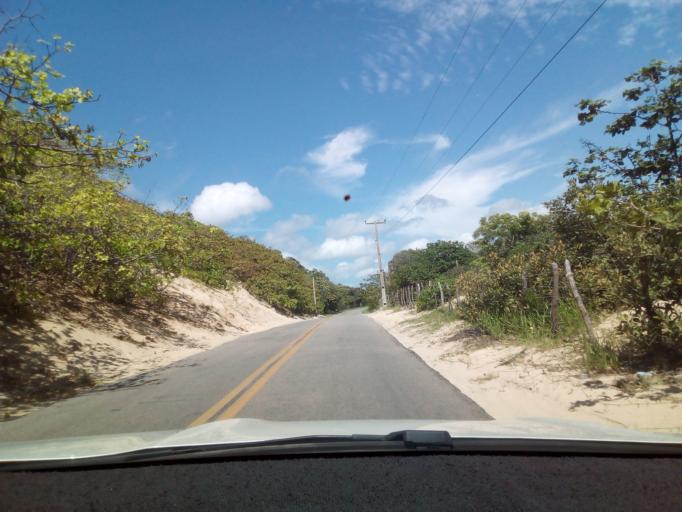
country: BR
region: Ceara
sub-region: Beberibe
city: Beberibe
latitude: -4.1824
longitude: -38.0881
